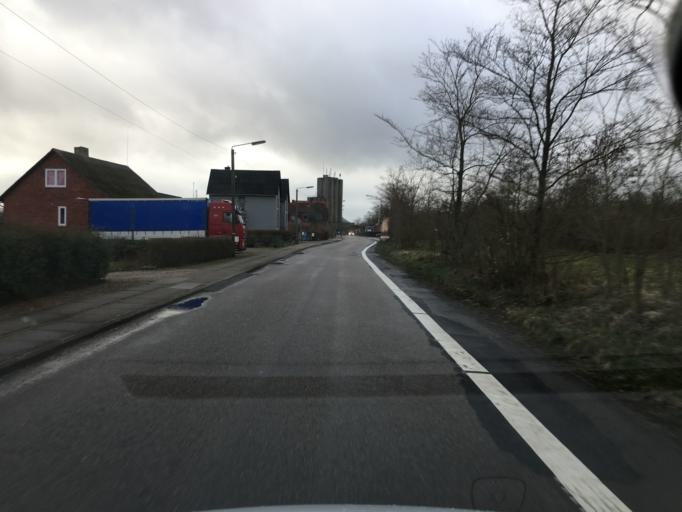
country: DE
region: Schleswig-Holstein
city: Bramstedtlund
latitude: 54.9424
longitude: 9.0917
